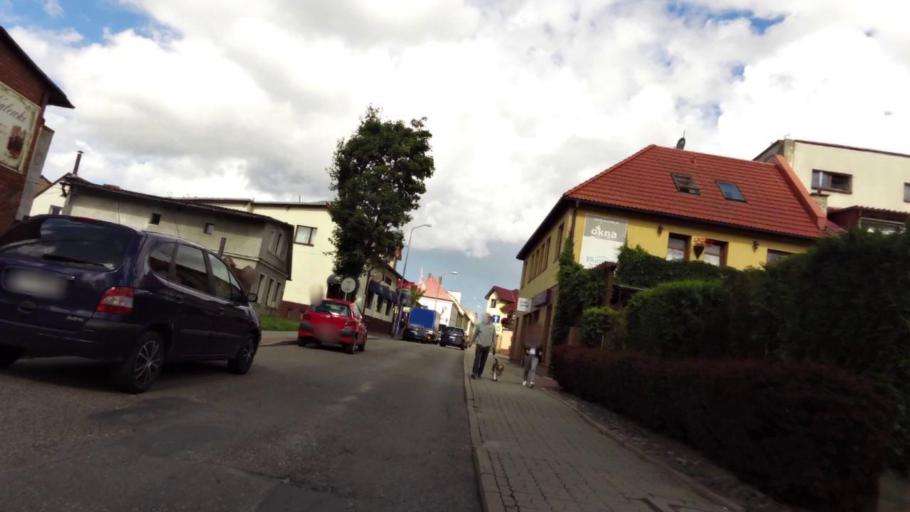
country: PL
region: West Pomeranian Voivodeship
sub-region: Powiat slawienski
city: Darlowo
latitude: 54.4212
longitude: 16.4134
